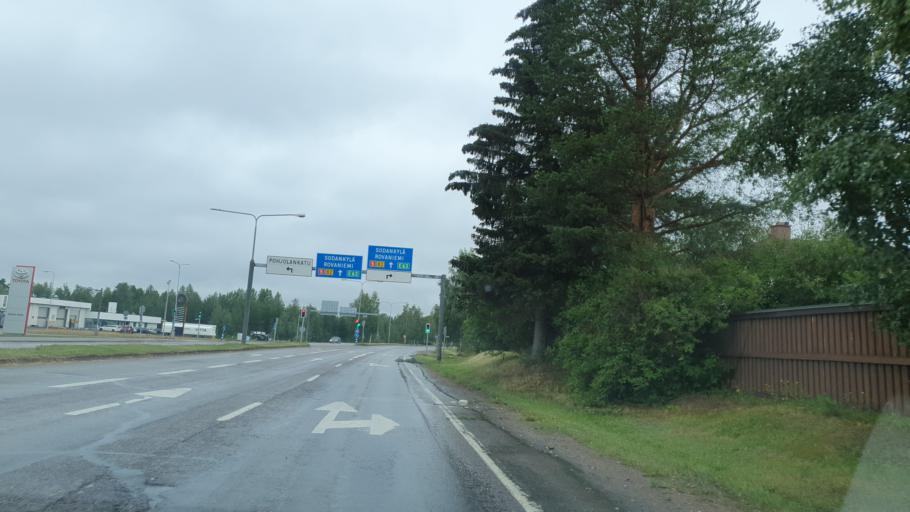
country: FI
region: Lapland
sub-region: Itae-Lappi
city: Kemijaervi
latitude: 66.7187
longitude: 27.4168
